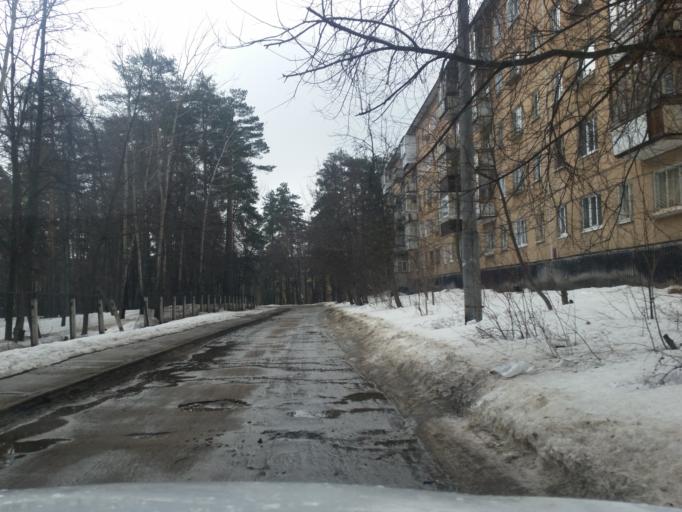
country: RU
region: Ulyanovsk
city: Dimitrovgrad
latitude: 54.2366
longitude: 49.5541
